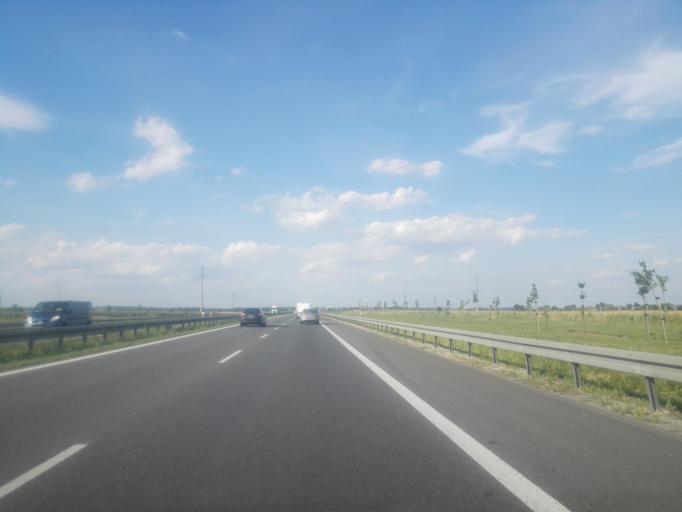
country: PL
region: Lower Silesian Voivodeship
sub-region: Powiat wroclawski
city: Mirkow
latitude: 51.2051
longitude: 17.1242
